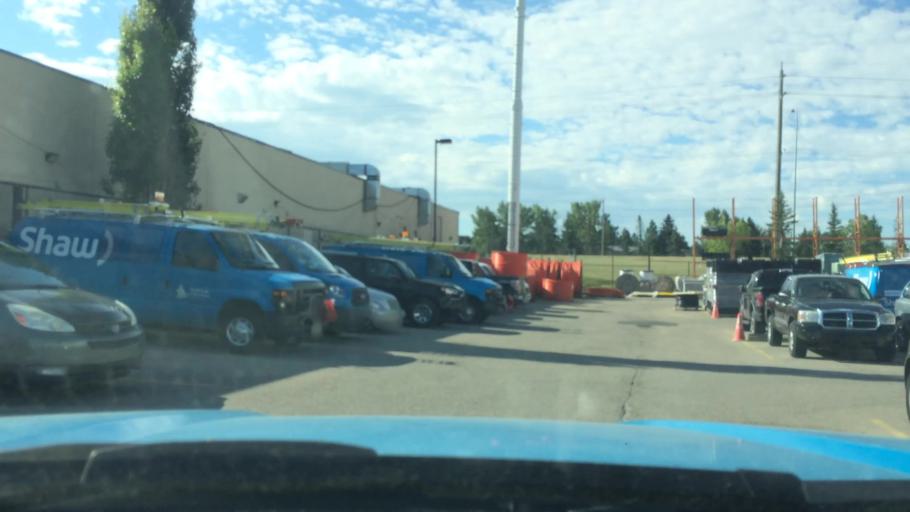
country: CA
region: Alberta
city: Calgary
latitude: 51.0972
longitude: -113.9632
